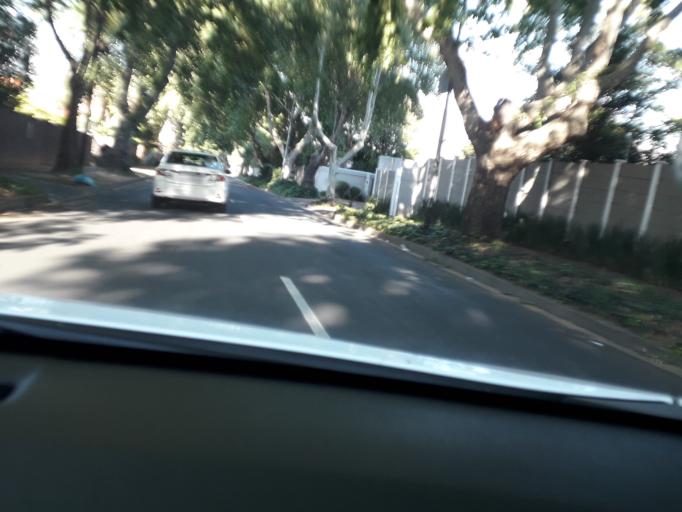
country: ZA
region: Gauteng
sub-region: City of Johannesburg Metropolitan Municipality
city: Johannesburg
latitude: -26.1451
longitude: 28.0829
